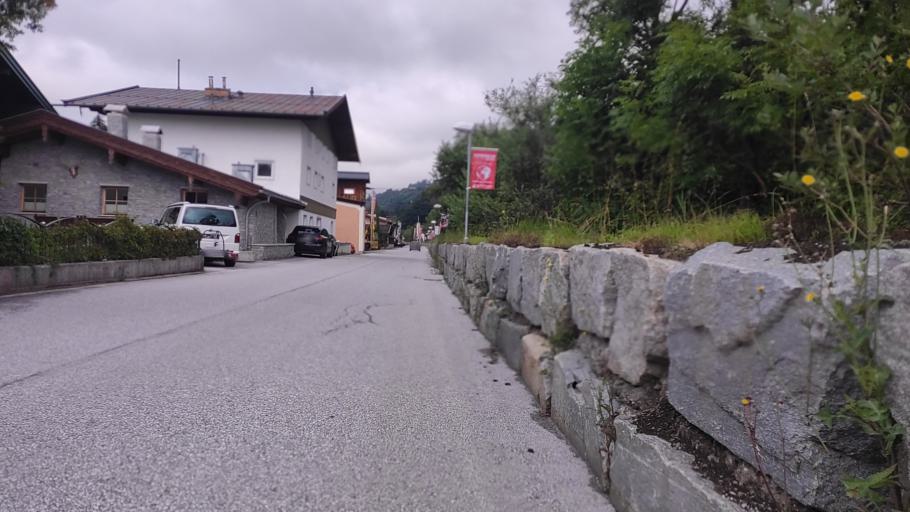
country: AT
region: Salzburg
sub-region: Politischer Bezirk Zell am See
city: Mittersill
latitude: 47.2833
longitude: 12.4787
